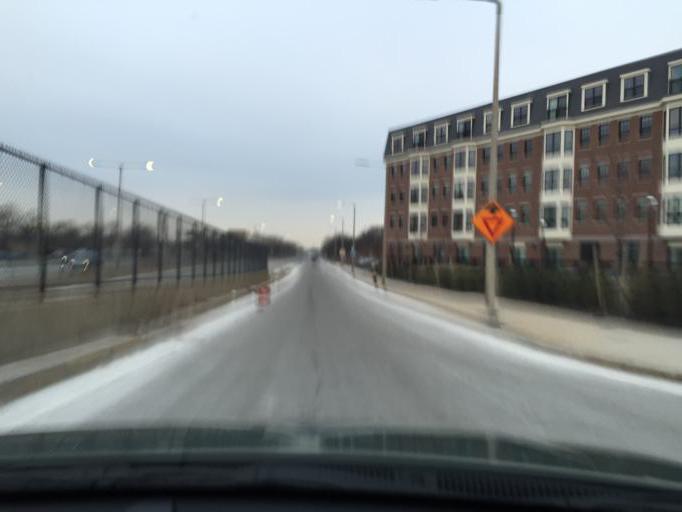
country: US
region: Massachusetts
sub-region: Suffolk County
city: Boston
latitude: 42.3751
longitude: -71.0680
